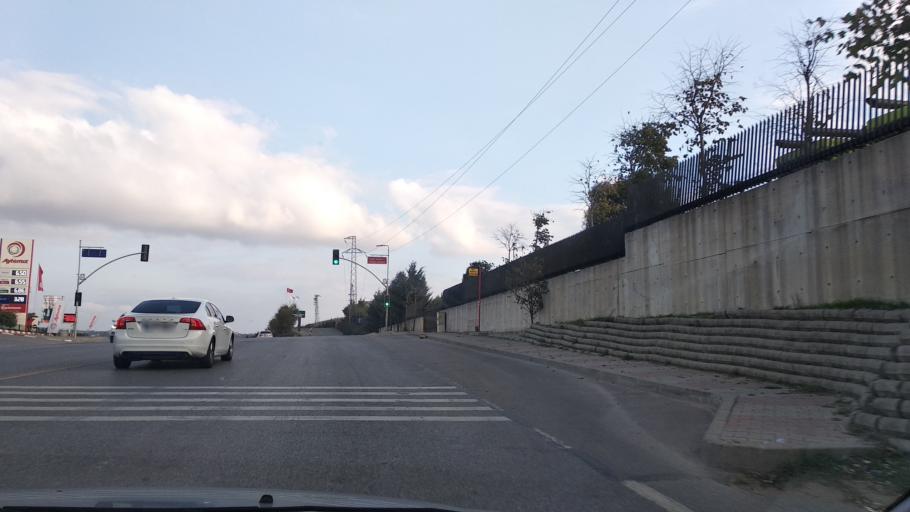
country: TR
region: Istanbul
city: Sultanbeyli
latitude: 40.9275
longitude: 29.3460
